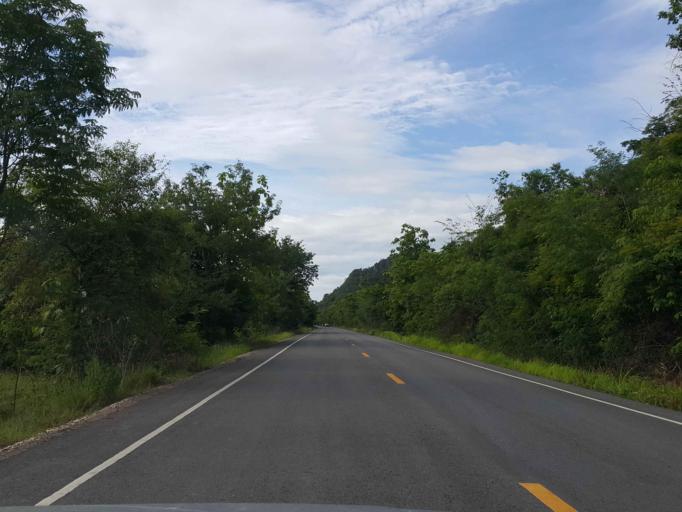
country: TH
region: Sukhothai
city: Thung Saliam
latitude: 17.2904
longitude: 99.5270
